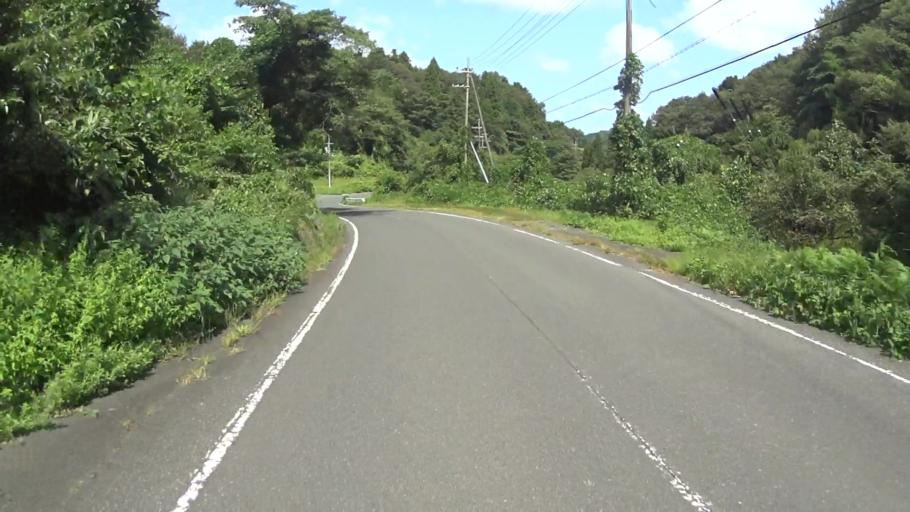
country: JP
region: Kyoto
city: Miyazu
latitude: 35.6783
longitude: 135.2499
